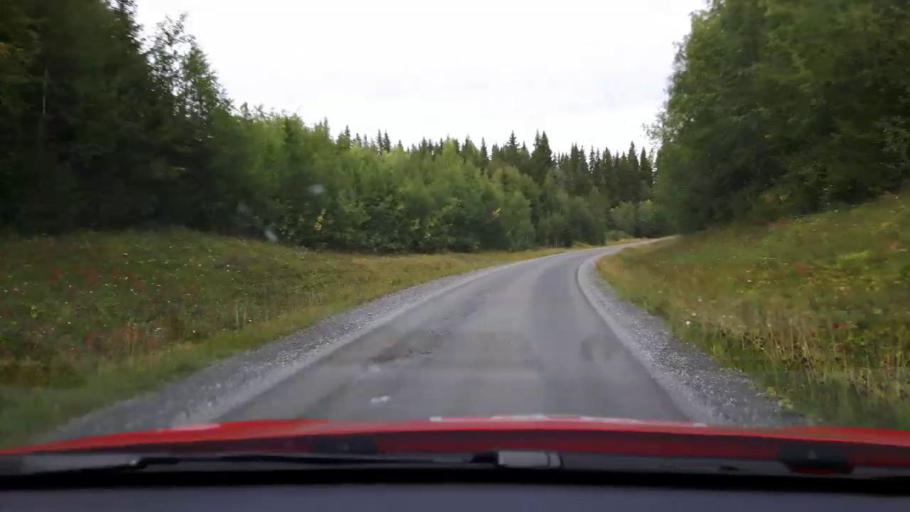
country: SE
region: Jaemtland
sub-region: Are Kommun
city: Are
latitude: 63.7493
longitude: 13.0881
